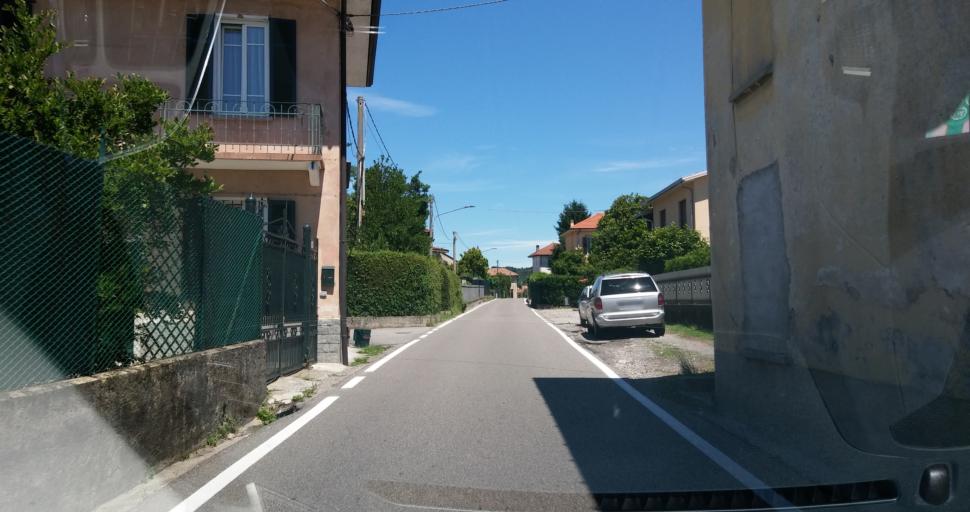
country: IT
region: Lombardy
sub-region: Provincia di Varese
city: Cimbro
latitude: 45.7466
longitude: 8.7255
